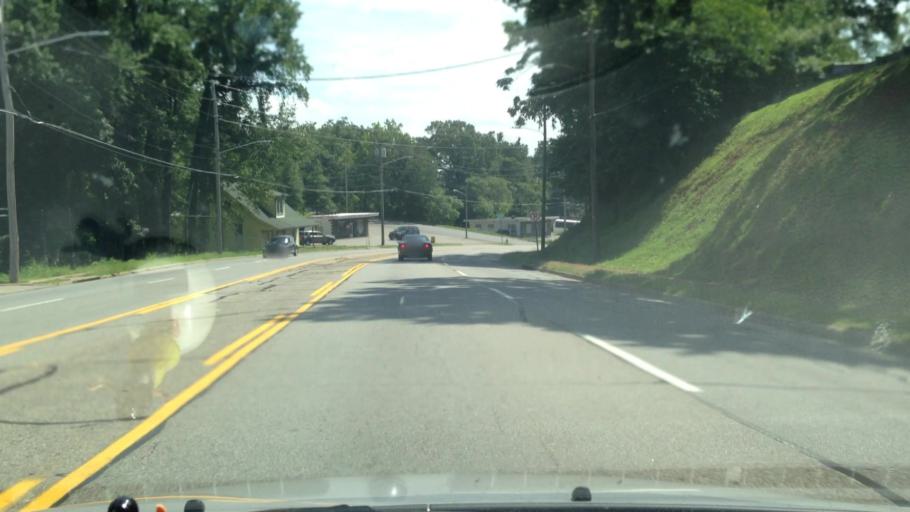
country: US
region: Virginia
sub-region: City of Martinsville
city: Martinsville
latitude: 36.6768
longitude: -79.8758
